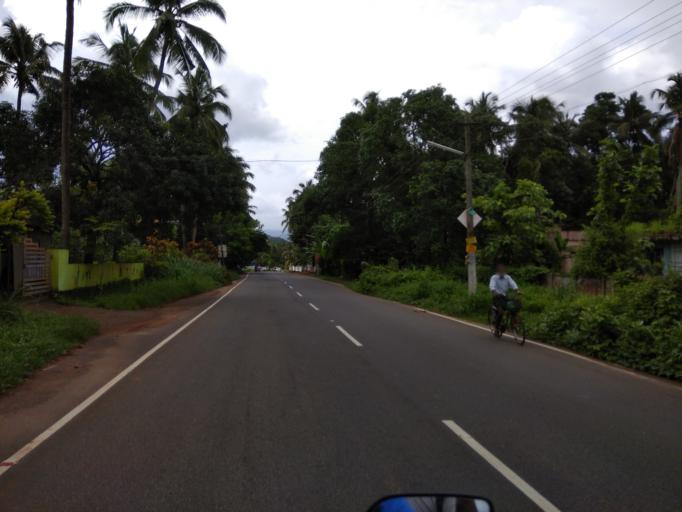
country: IN
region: Kerala
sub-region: Thrissur District
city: Trichur
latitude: 10.5413
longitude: 76.3304
